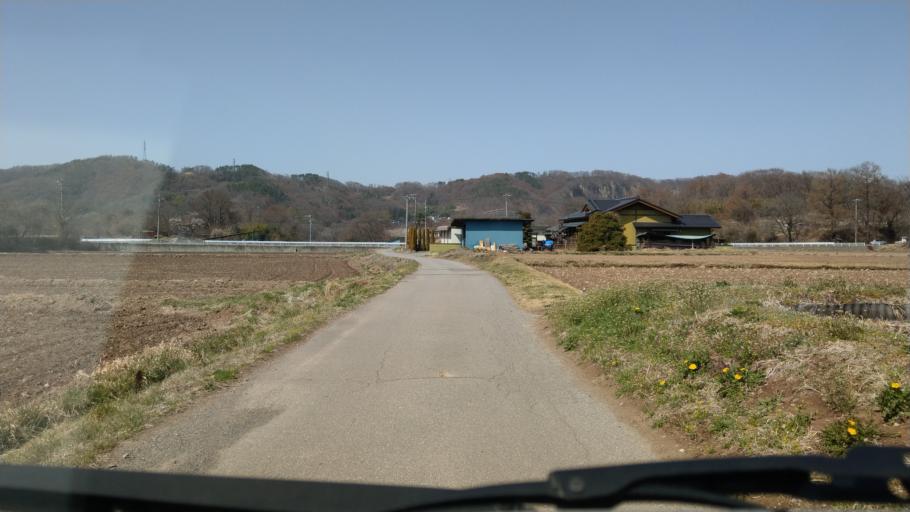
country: JP
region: Nagano
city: Komoro
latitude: 36.3005
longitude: 138.4322
